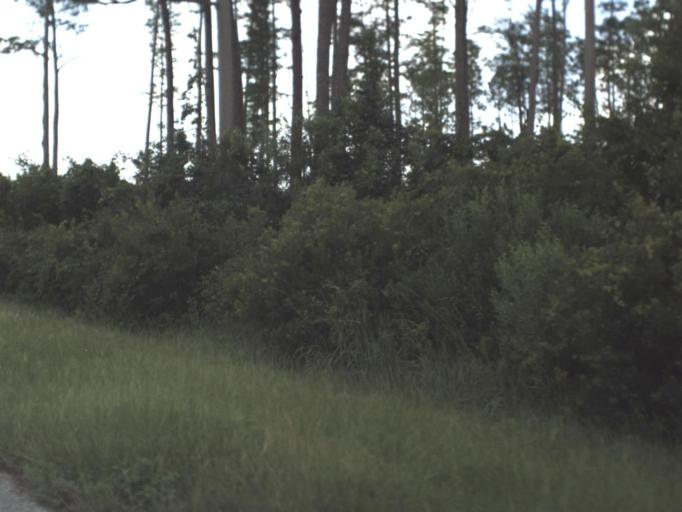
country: US
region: Florida
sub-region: Baker County
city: Macclenny
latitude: 30.5303
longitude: -82.3105
